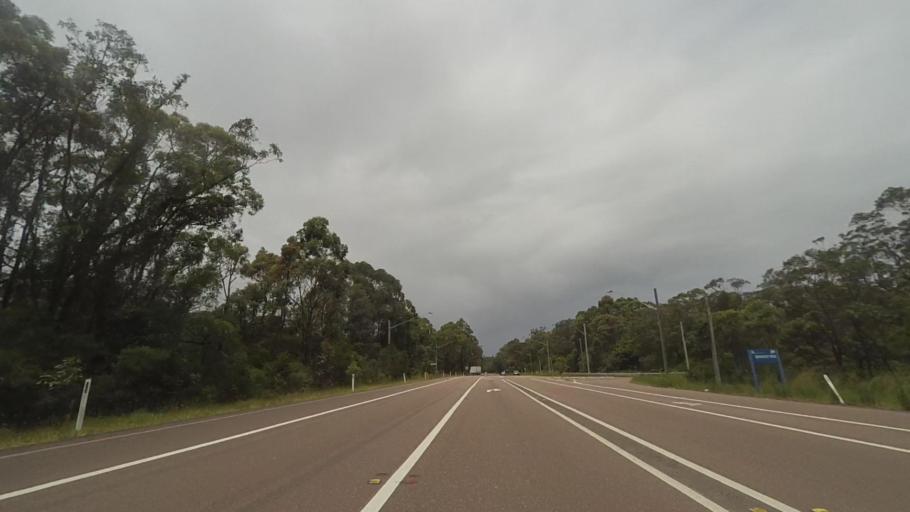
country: AU
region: New South Wales
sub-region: Wyong Shire
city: Chittaway Bay
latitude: -33.3304
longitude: 151.4111
